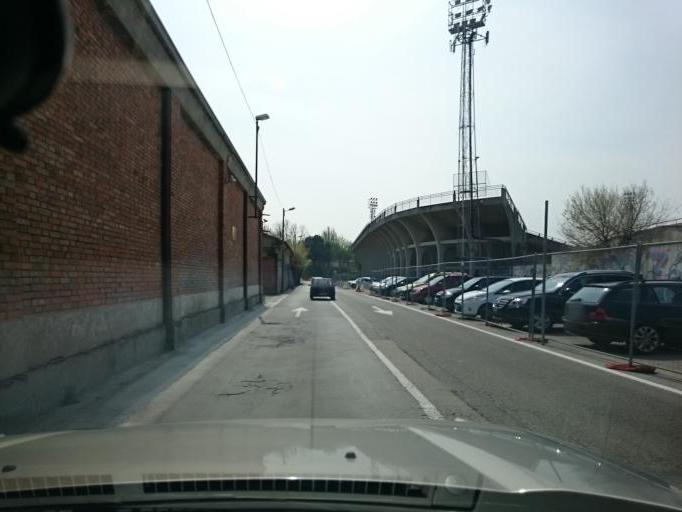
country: IT
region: Veneto
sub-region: Provincia di Padova
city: Padova
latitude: 45.3949
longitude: 11.8766
